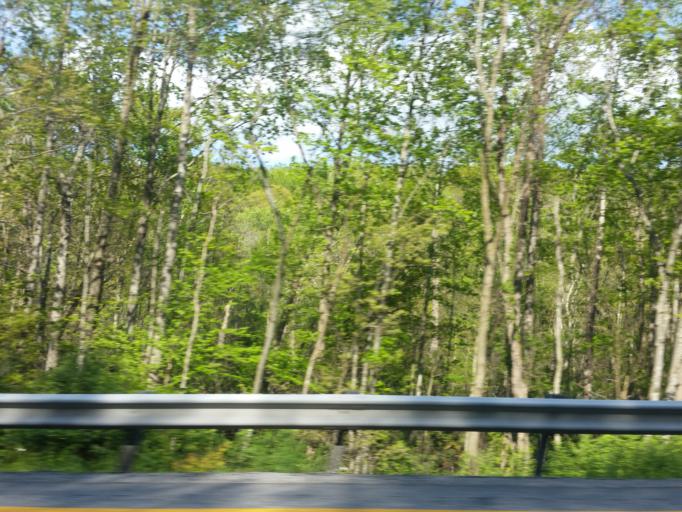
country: US
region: West Virginia
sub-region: Raleigh County
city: Shady Spring
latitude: 37.6884
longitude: -81.1296
